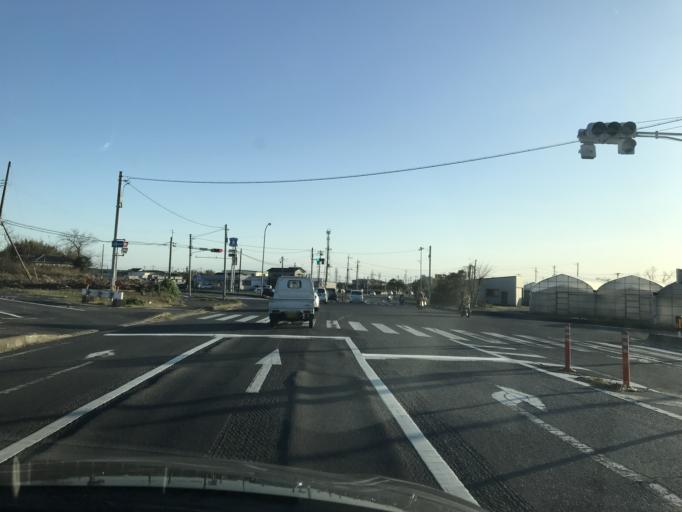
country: JP
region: Chiba
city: Omigawa
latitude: 35.8801
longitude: 140.6307
